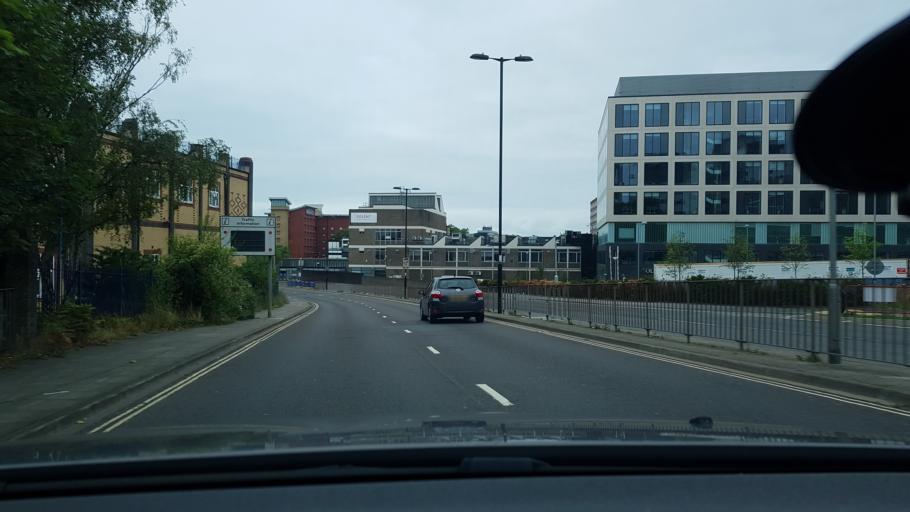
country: GB
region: England
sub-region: Southampton
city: Southampton
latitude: 50.9095
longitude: -1.4003
